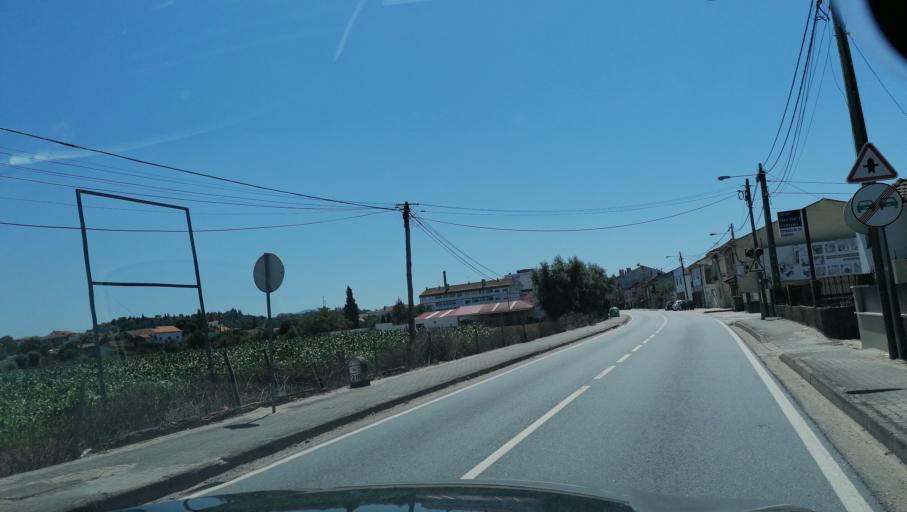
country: PT
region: Aveiro
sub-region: Anadia
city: Arcos
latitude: 40.4541
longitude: -8.4538
